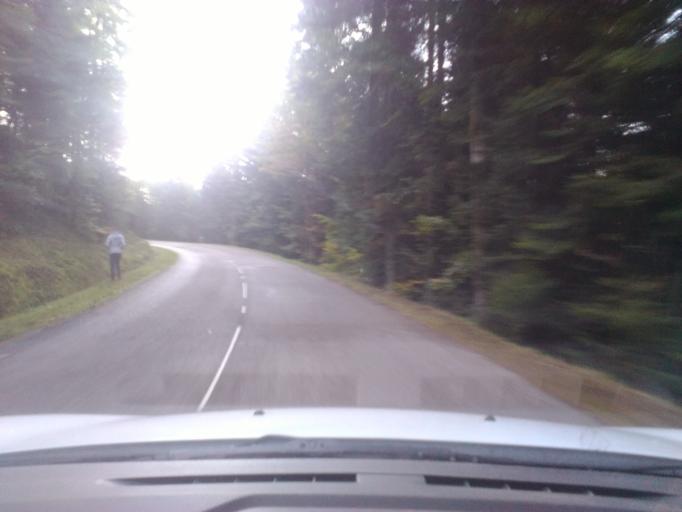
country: FR
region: Lorraine
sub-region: Departement des Vosges
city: Etival-Clairefontaine
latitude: 48.3019
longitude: 6.7954
